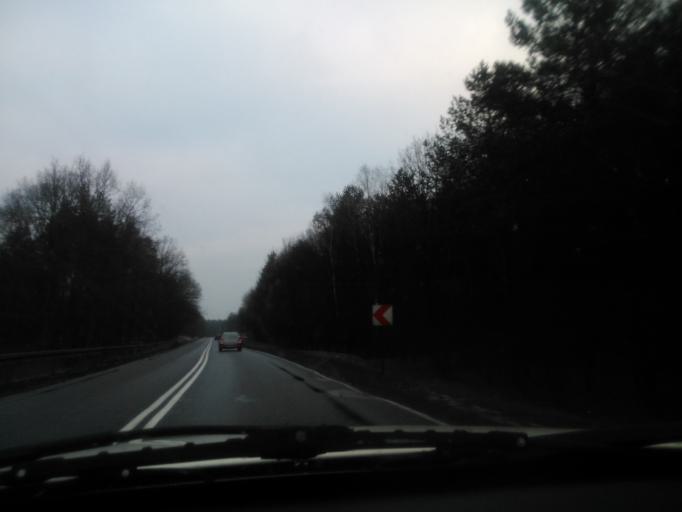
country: PL
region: Kujawsko-Pomorskie
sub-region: Powiat torunski
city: Lubicz Gorny
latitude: 53.1089
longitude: 18.8031
